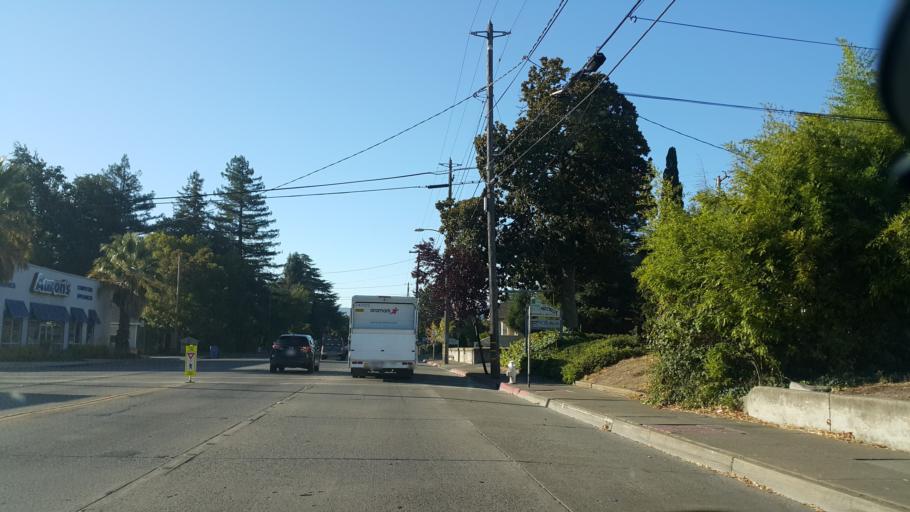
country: US
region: California
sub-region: Mendocino County
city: Ukiah
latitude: 39.1570
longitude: -123.2085
